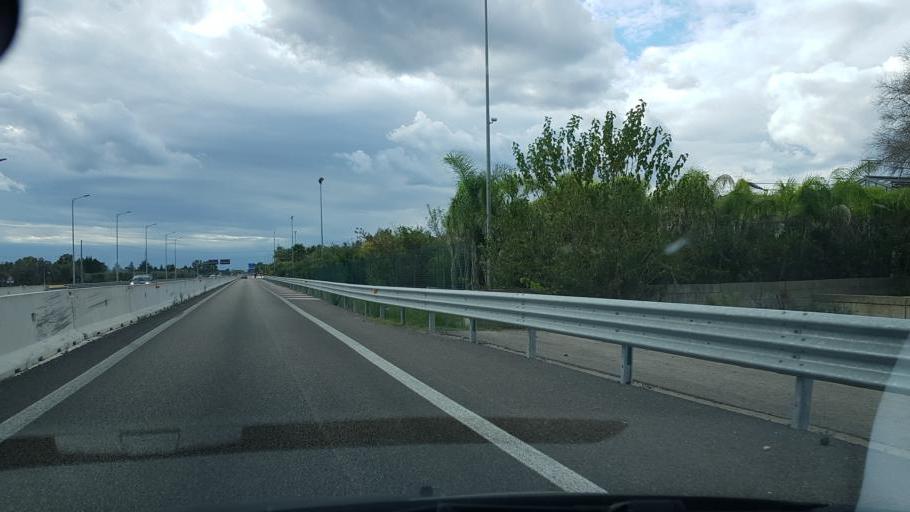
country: IT
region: Apulia
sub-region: Provincia di Lecce
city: Muro Leccese
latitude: 40.1247
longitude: 18.3345
